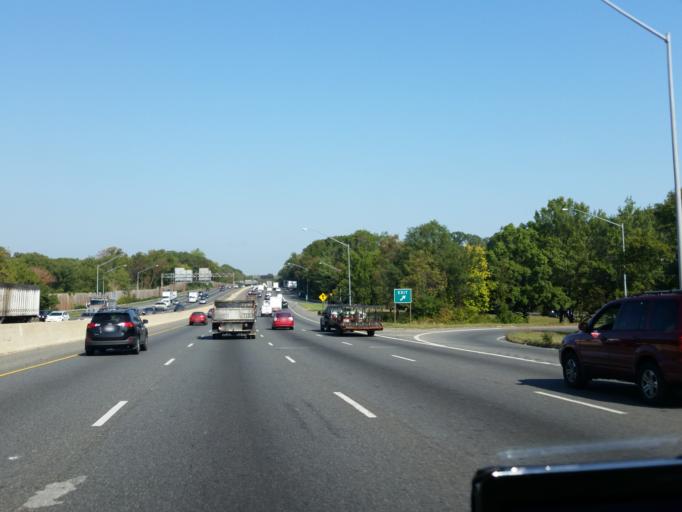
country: US
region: Maryland
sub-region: Prince George's County
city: Lanham
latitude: 38.9604
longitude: -76.8664
